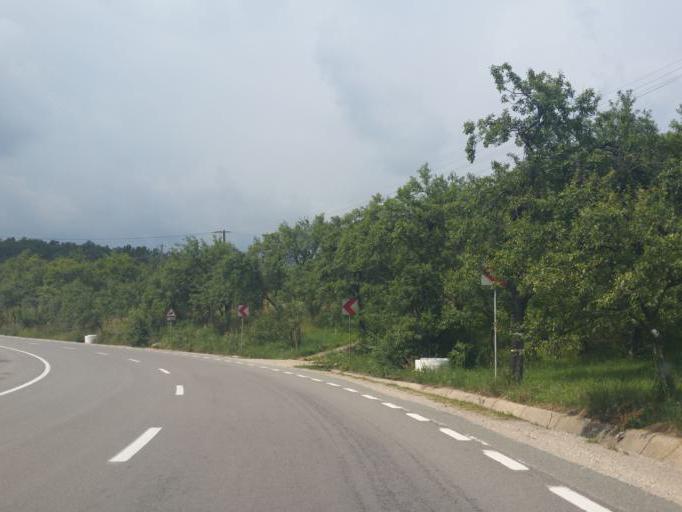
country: RO
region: Salaj
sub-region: Comuna Treznea
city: Treznea
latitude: 47.1325
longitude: 23.1307
